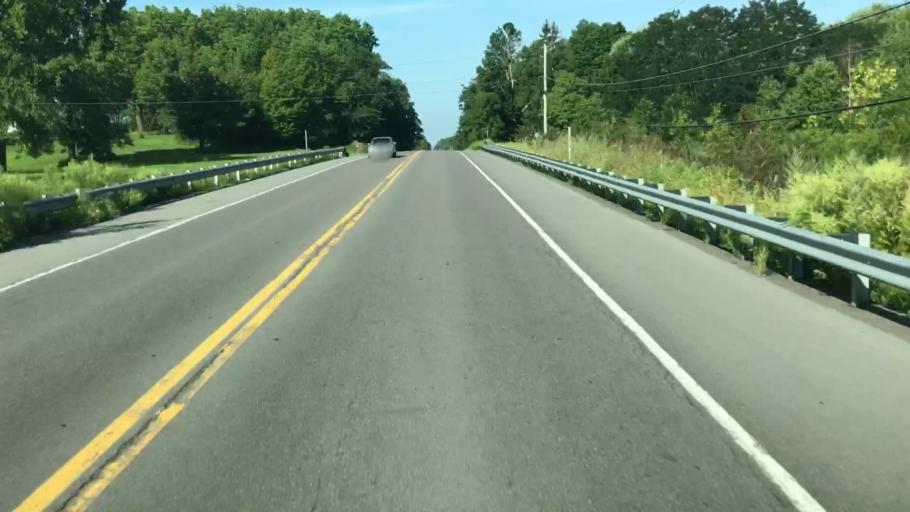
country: US
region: New York
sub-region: Onondaga County
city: Skaneateles
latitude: 42.9416
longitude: -76.4808
